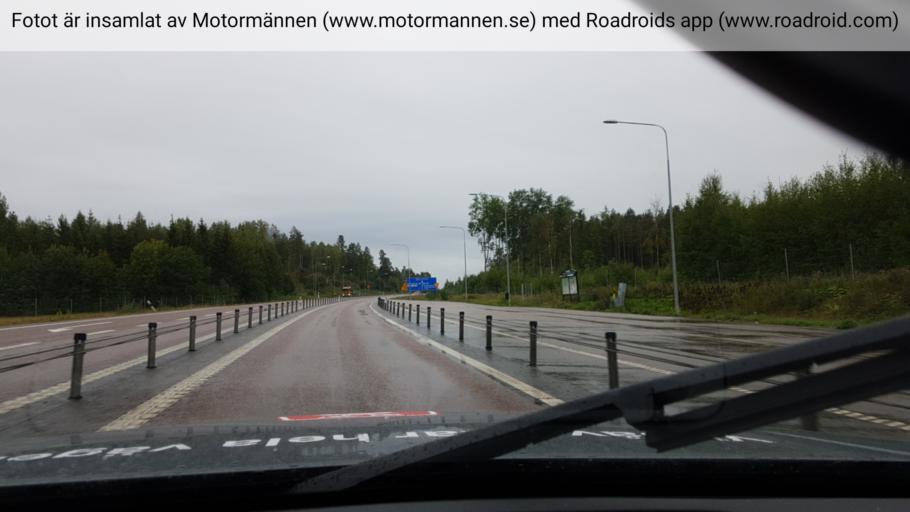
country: SE
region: Soedermanland
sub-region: Flens Kommun
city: Malmkoping
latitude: 59.1435
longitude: 16.7122
